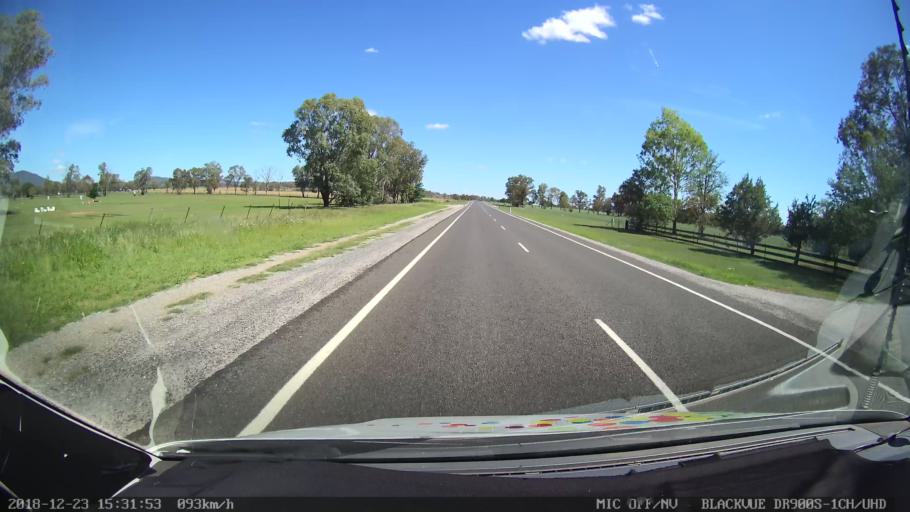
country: AU
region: New South Wales
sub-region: Tamworth Municipality
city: East Tamworth
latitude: -30.9779
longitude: 150.8690
